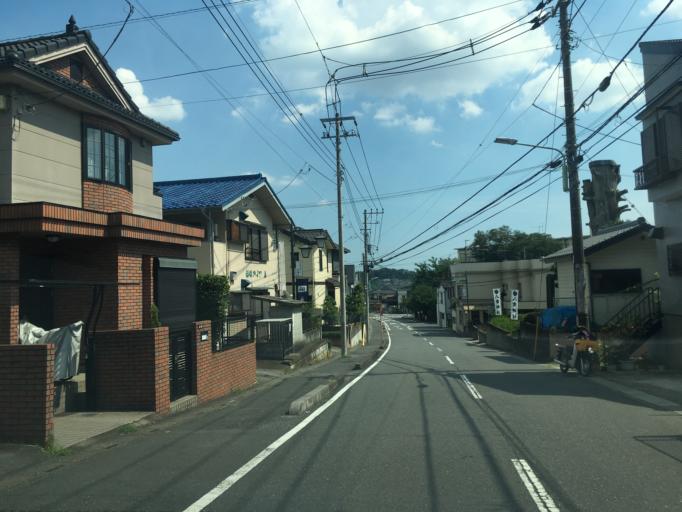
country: JP
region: Saitama
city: Tokorozawa
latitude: 35.7837
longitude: 139.4397
